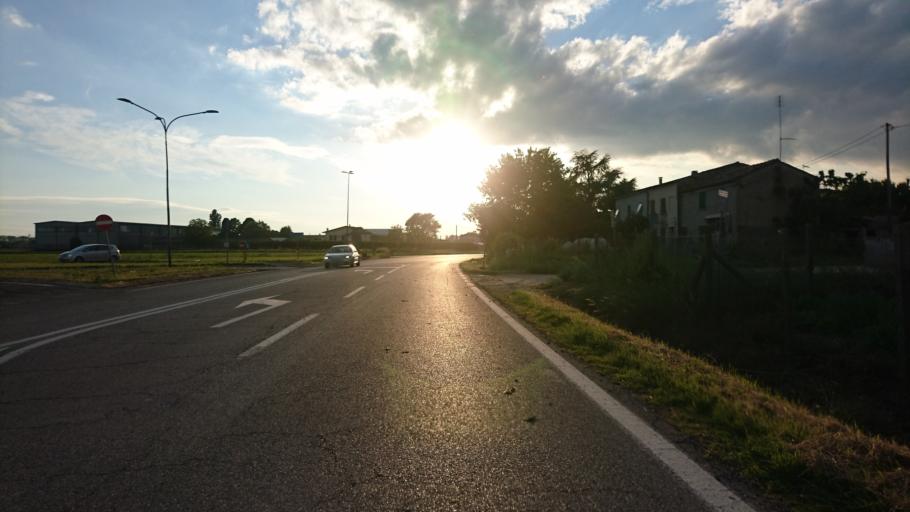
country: IT
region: Veneto
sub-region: Provincia di Rovigo
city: Castelmassa
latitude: 45.0174
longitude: 11.3294
